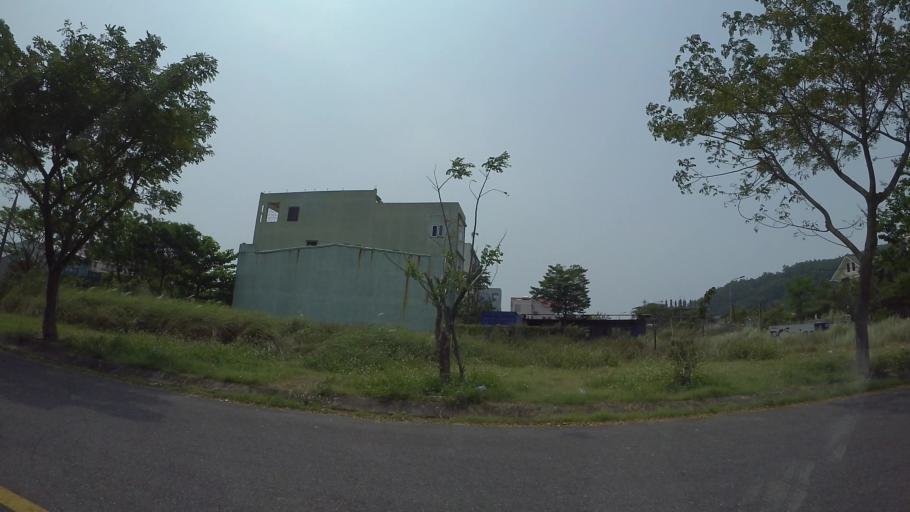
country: VN
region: Da Nang
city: Son Tra
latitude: 16.1072
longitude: 108.2610
